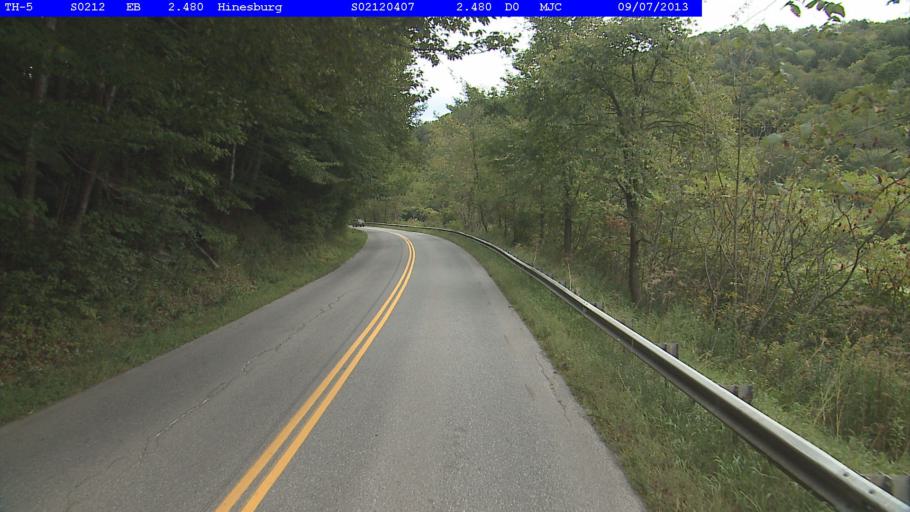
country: US
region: Vermont
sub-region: Chittenden County
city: Hinesburg
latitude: 44.2882
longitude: -73.0228
